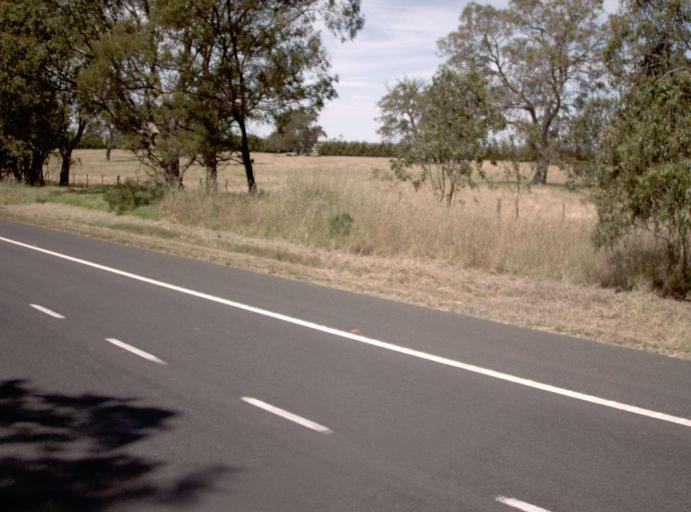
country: AU
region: Victoria
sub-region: Latrobe
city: Traralgon
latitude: -38.1641
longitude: 146.7020
